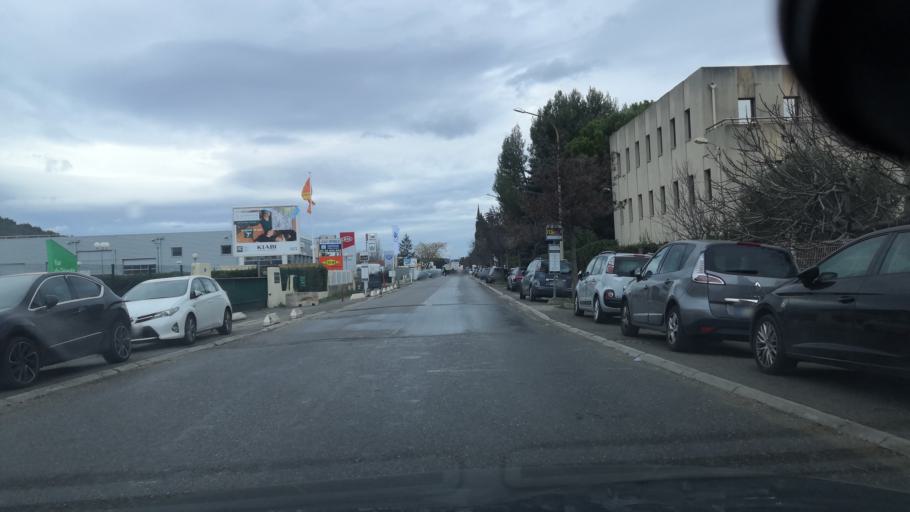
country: FR
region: Provence-Alpes-Cote d'Azur
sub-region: Departement des Bouches-du-Rhone
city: Gemenos
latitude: 43.2826
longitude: 5.6075
